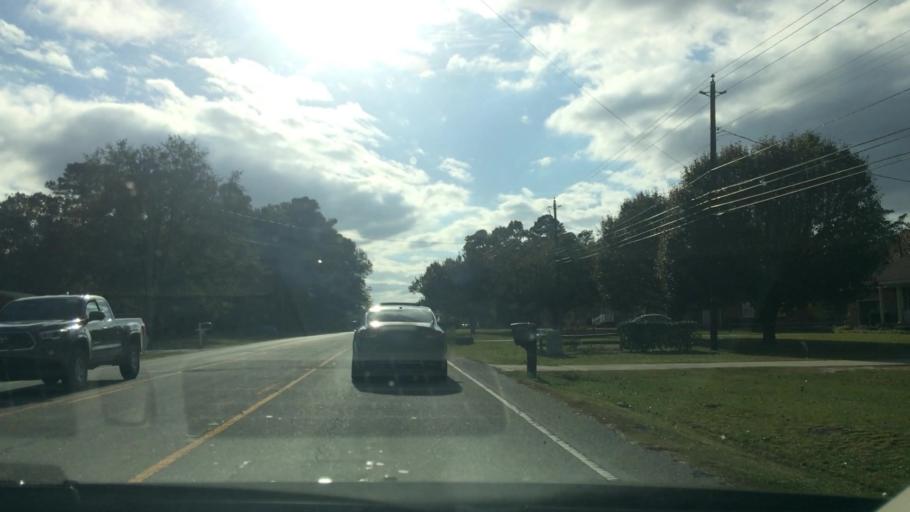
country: US
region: North Carolina
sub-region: Wayne County
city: Elroy
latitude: 35.3909
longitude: -77.9167
